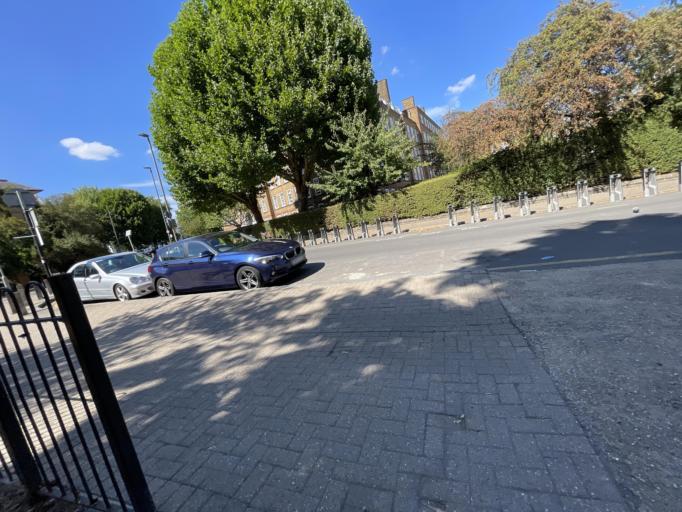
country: GB
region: England
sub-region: Greater London
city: Chelsea
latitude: 51.4728
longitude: -0.1764
